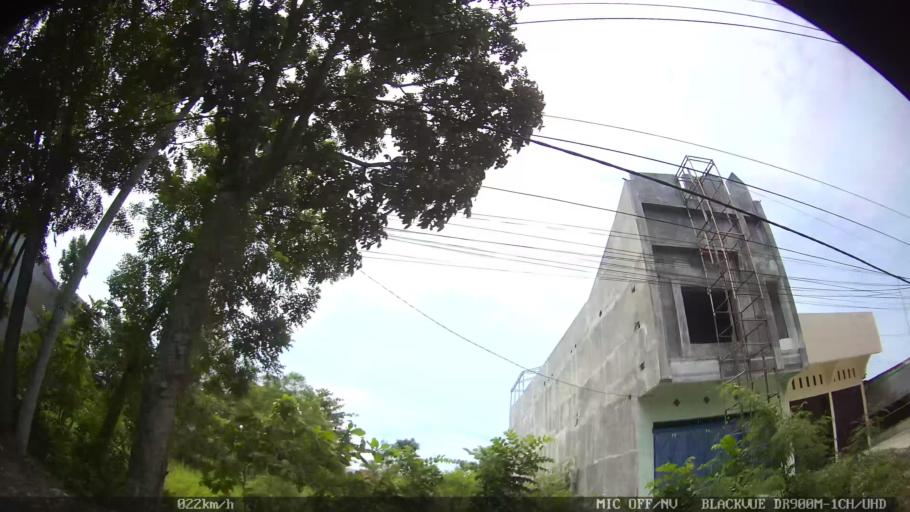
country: ID
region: North Sumatra
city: Medan
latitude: 3.5550
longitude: 98.6537
